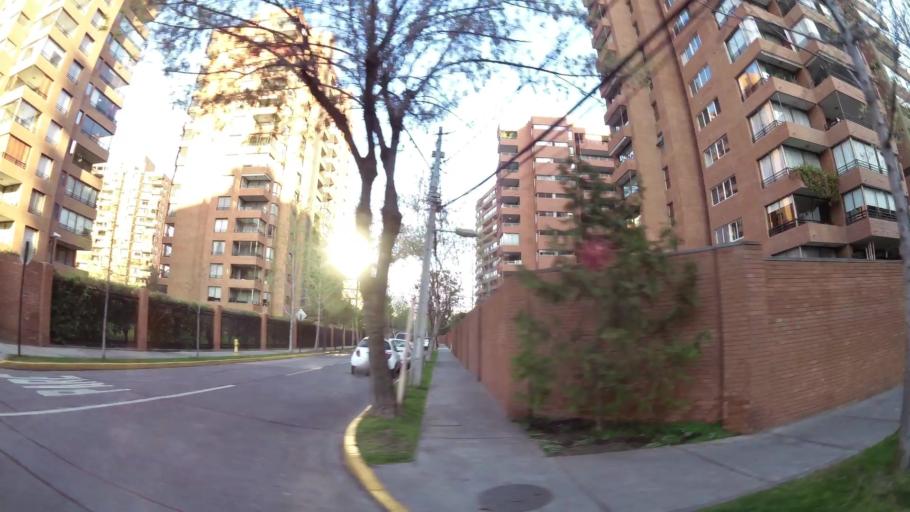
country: CL
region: Santiago Metropolitan
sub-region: Provincia de Santiago
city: Villa Presidente Frei, Nunoa, Santiago, Chile
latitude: -33.4033
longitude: -70.5625
